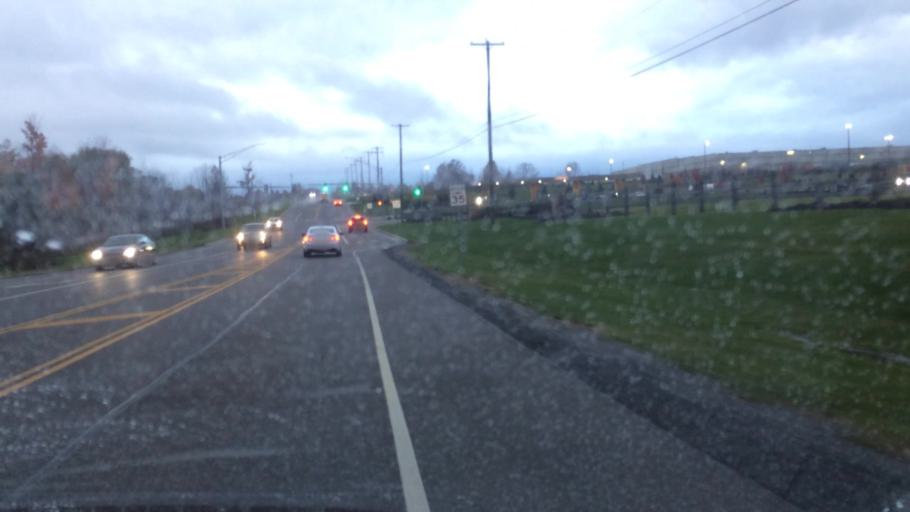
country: US
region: Ohio
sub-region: Summit County
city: Boston Heights
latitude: 41.2632
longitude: -81.5051
